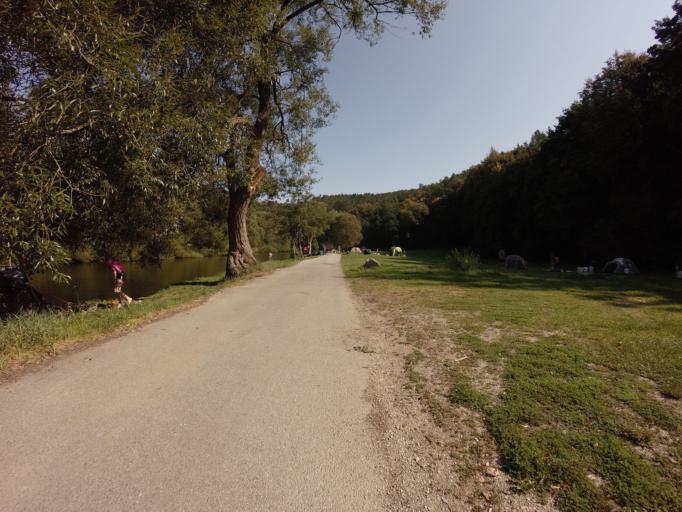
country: CZ
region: Jihocesky
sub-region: Okres Cesky Krumlov
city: Cesky Krumlov
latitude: 48.8547
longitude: 14.3731
